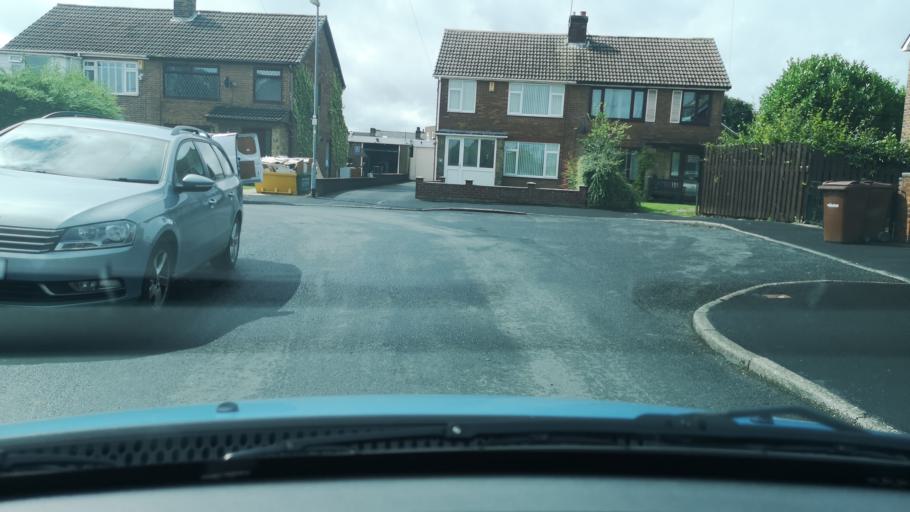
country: GB
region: England
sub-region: City and Borough of Wakefield
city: Low Ackworth
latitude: 53.6426
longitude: -1.3466
